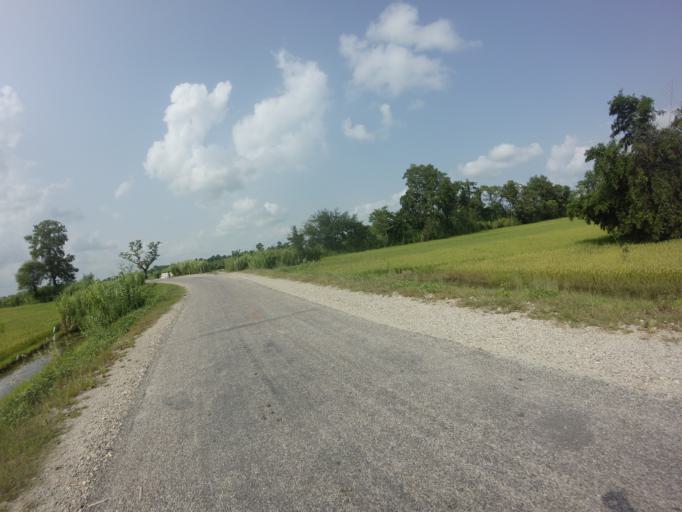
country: NP
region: Far Western
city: Tikapur
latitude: 28.4694
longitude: 81.0741
